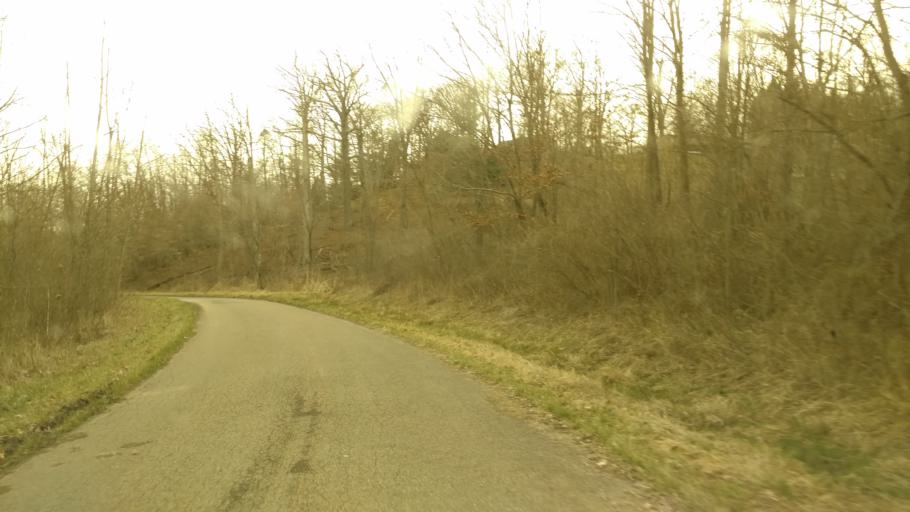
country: US
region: Ohio
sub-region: Muskingum County
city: Frazeysburg
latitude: 40.0276
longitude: -82.1196
